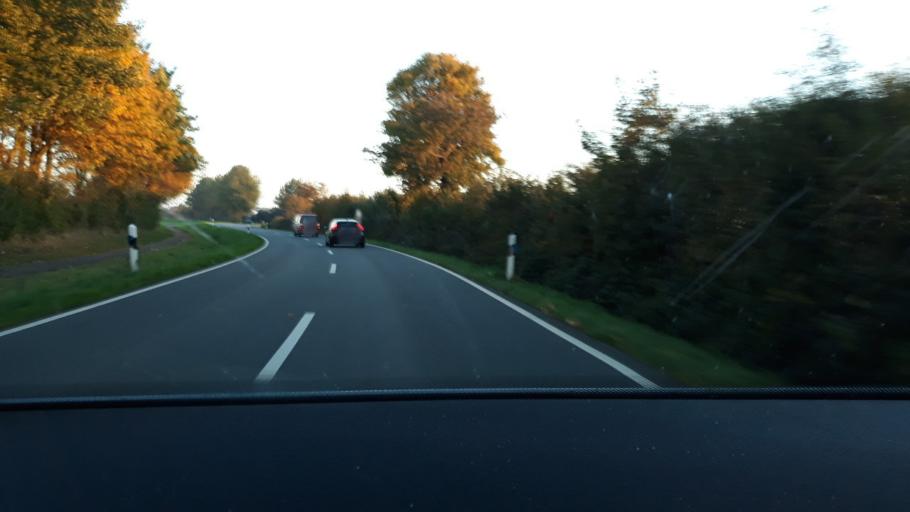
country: DE
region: Schleswig-Holstein
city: Ulsby
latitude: 54.6235
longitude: 9.5965
